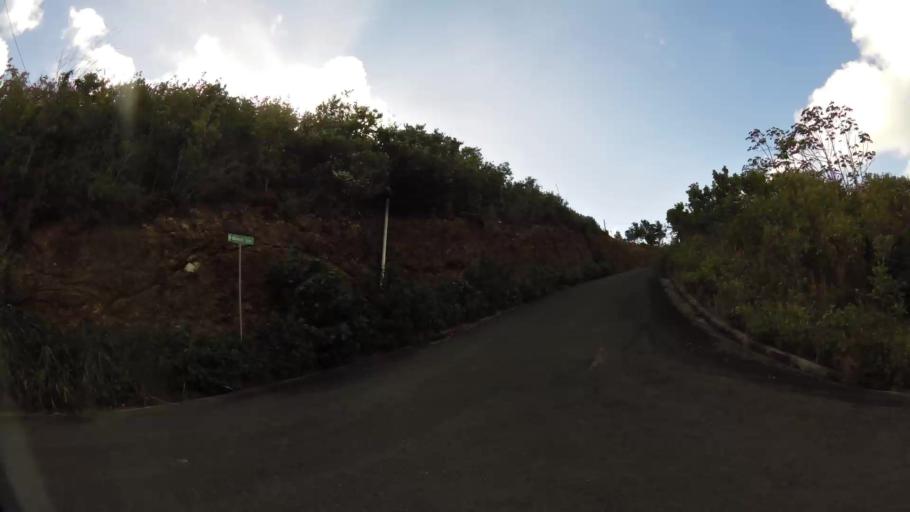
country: LC
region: Castries Quarter
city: Bisee
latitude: 14.0385
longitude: -60.9566
